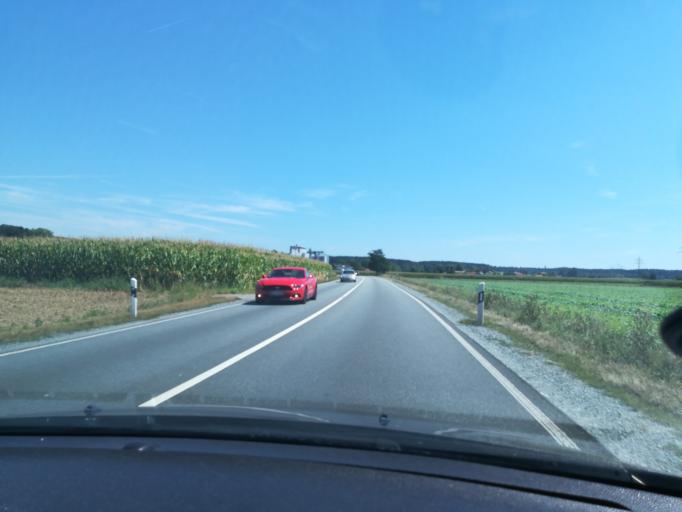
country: DE
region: Bavaria
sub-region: Upper Bavaria
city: Hohenlinden
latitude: 48.1483
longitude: 12.0052
